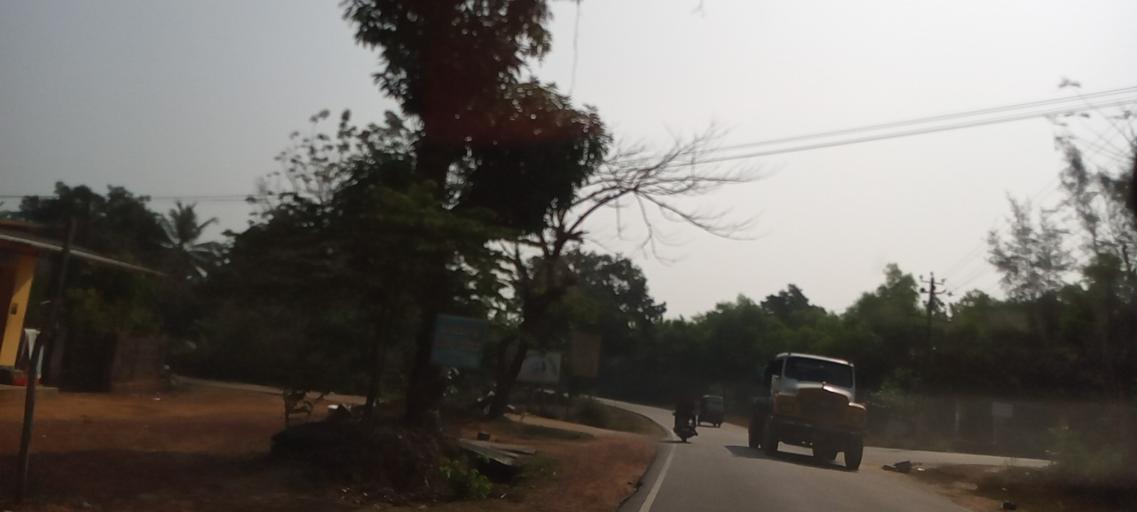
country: IN
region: Karnataka
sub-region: Udupi
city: Coondapoor
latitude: 13.5118
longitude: 74.7811
